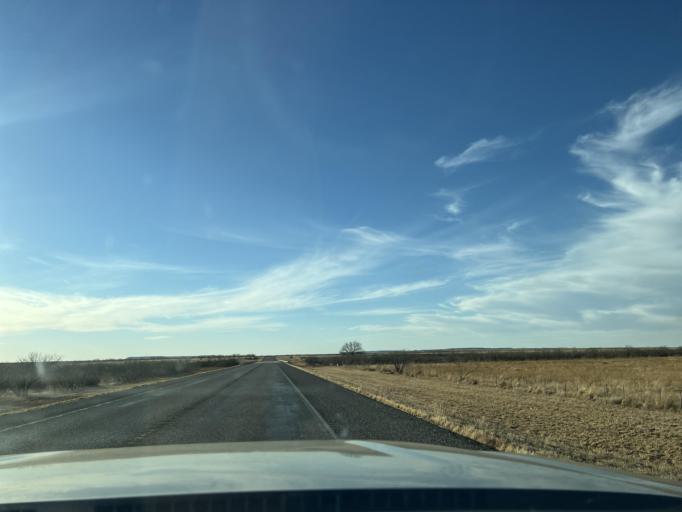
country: US
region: Texas
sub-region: Borden County
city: Gail
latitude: 32.7708
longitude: -101.3340
